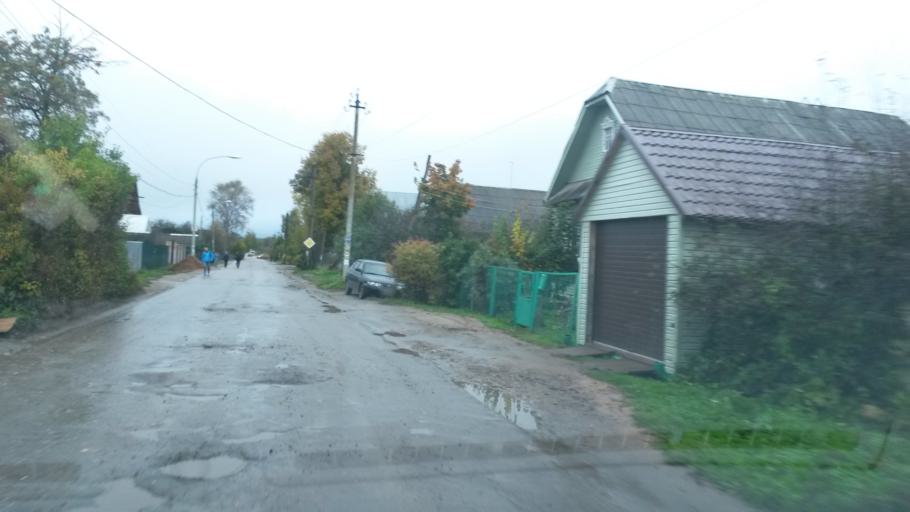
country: RU
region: Jaroslavl
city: Gavrilov-Yam
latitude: 57.3099
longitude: 39.8565
